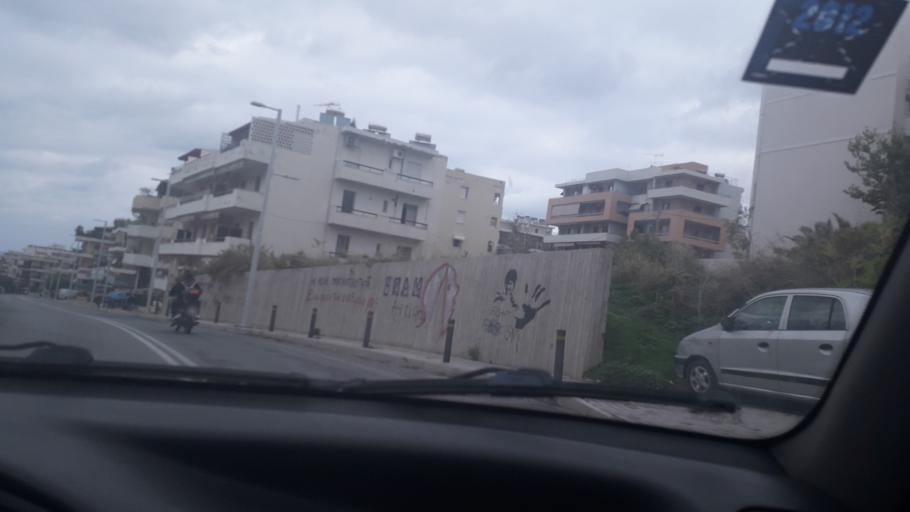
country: GR
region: Crete
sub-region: Nomos Rethymnis
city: Rethymno
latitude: 35.3594
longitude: 24.4753
